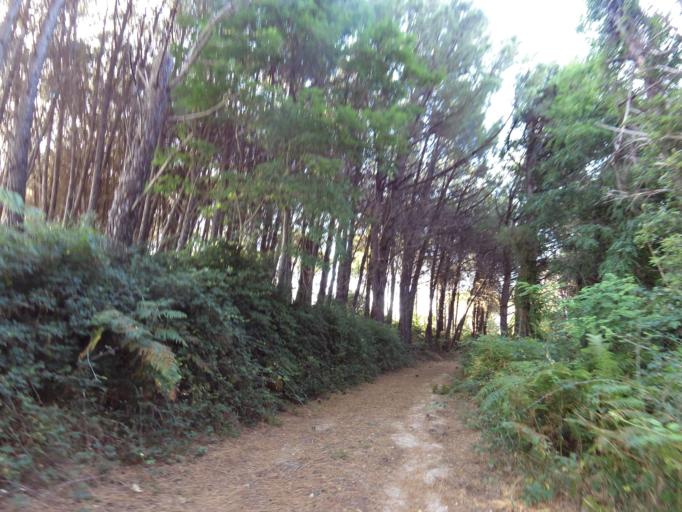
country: IT
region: Calabria
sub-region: Provincia di Reggio Calabria
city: Pazzano
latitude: 38.4676
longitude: 16.4137
